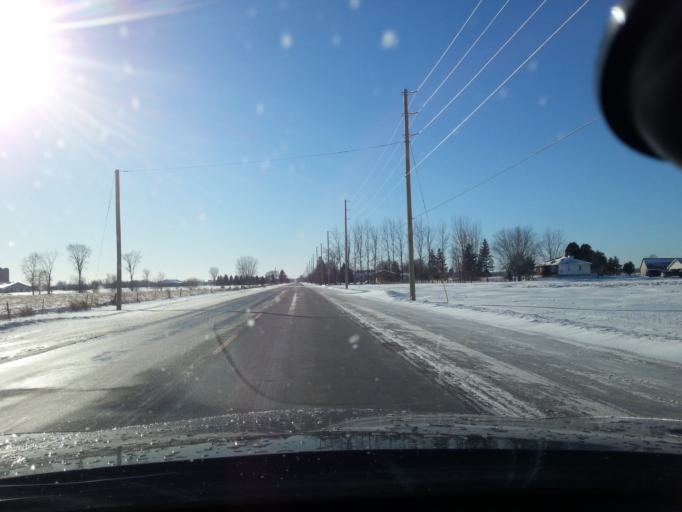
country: CA
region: Ontario
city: Ottawa
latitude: 45.3122
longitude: -75.4927
